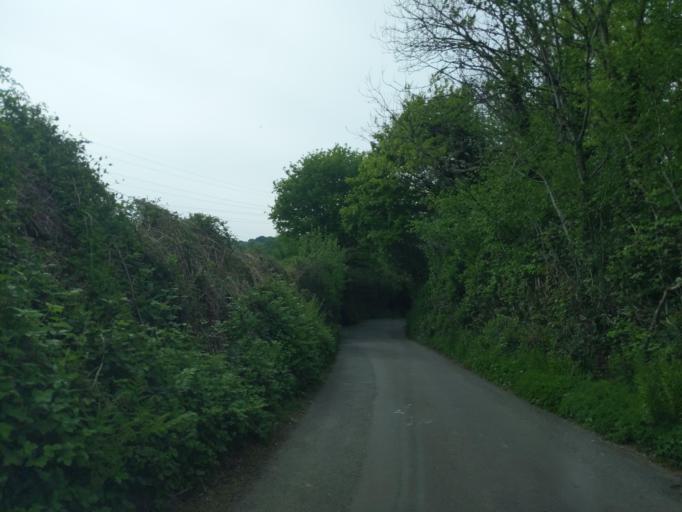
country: GB
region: England
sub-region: Devon
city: Plympton
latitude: 50.4319
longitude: -4.0576
